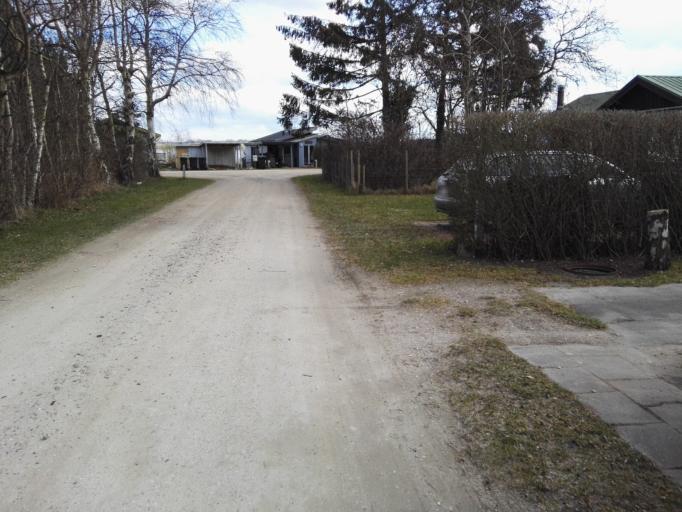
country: DK
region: Zealand
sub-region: Lejre Kommune
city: Ejby
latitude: 55.7621
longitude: 11.8310
